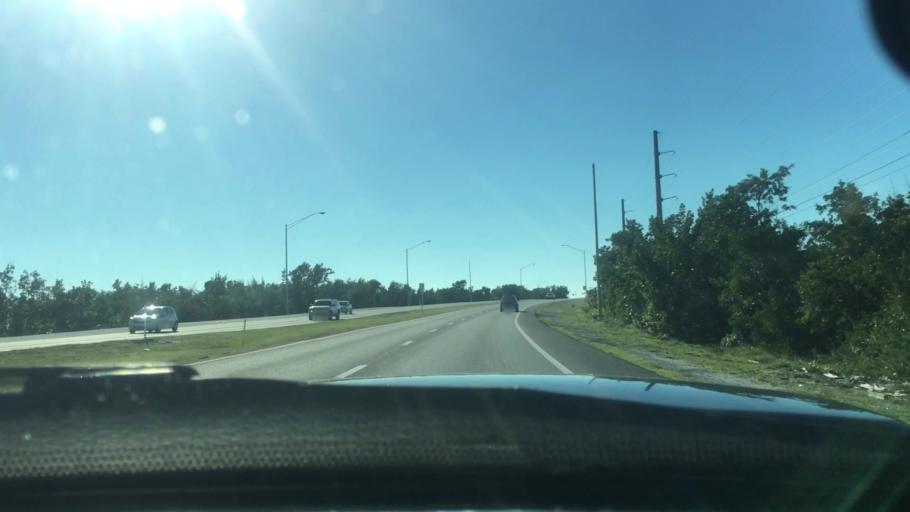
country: US
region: Florida
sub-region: Monroe County
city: Stock Island
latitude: 24.5793
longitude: -81.7085
